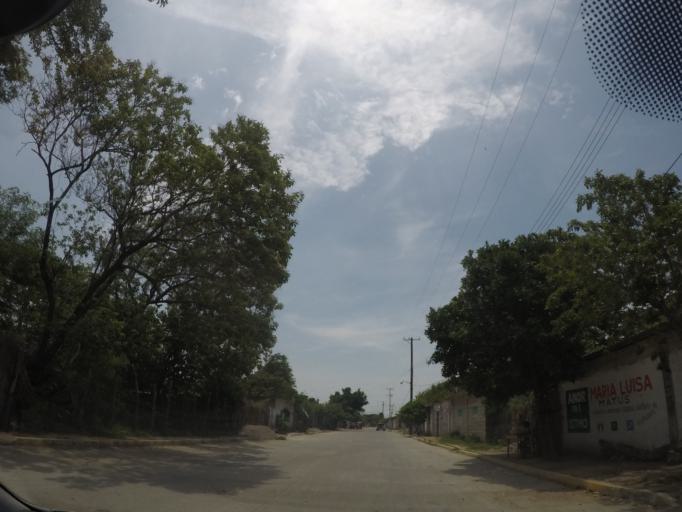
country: MX
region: Oaxaca
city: San Mateo del Mar
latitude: 16.2107
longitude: -94.9861
